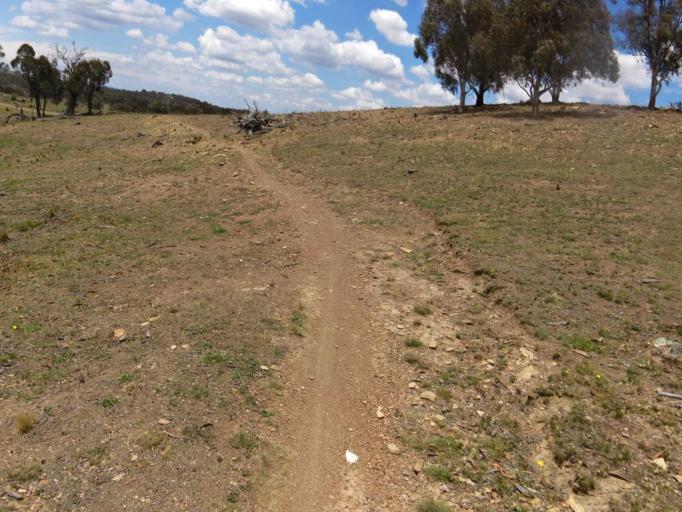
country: AU
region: Australian Capital Territory
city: Kaleen
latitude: -35.1344
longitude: 149.1379
